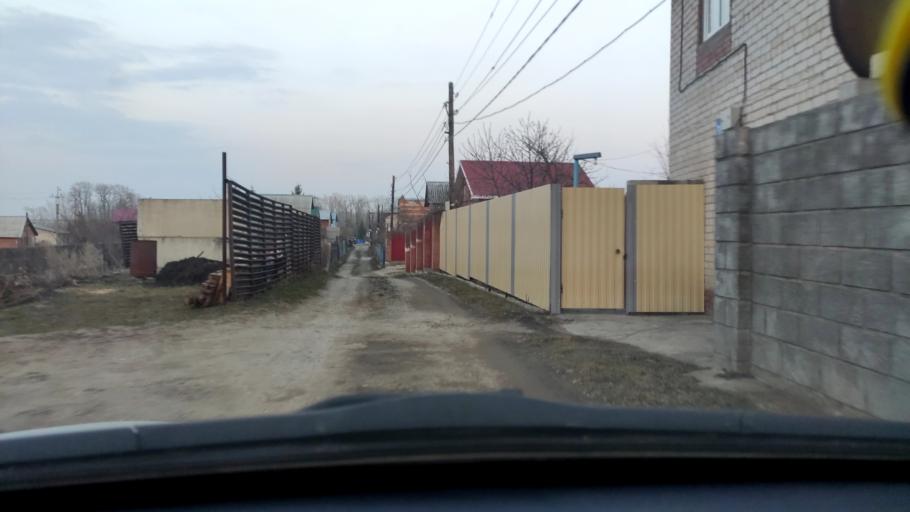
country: RU
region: Samara
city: Zhigulevsk
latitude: 53.4528
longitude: 49.5231
